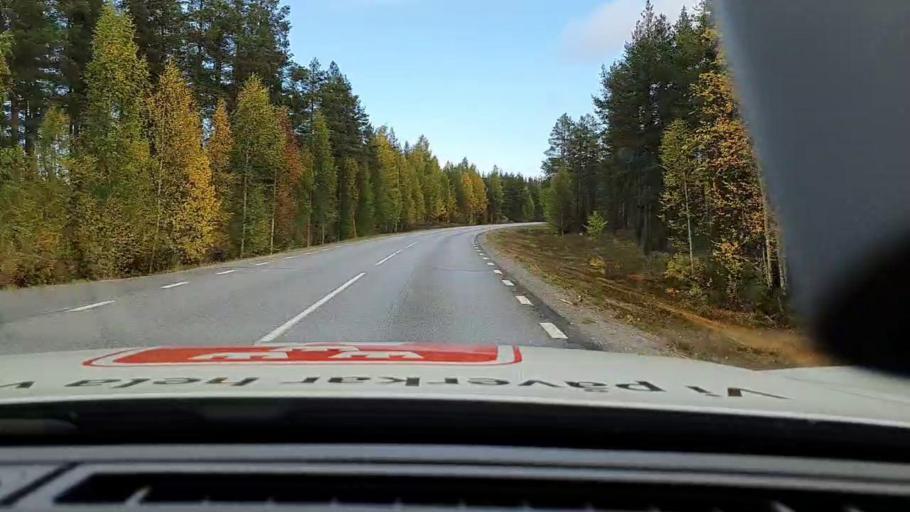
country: SE
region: Vaesterbotten
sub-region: Norsjo Kommun
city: Norsjoe
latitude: 64.9630
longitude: 19.6967
